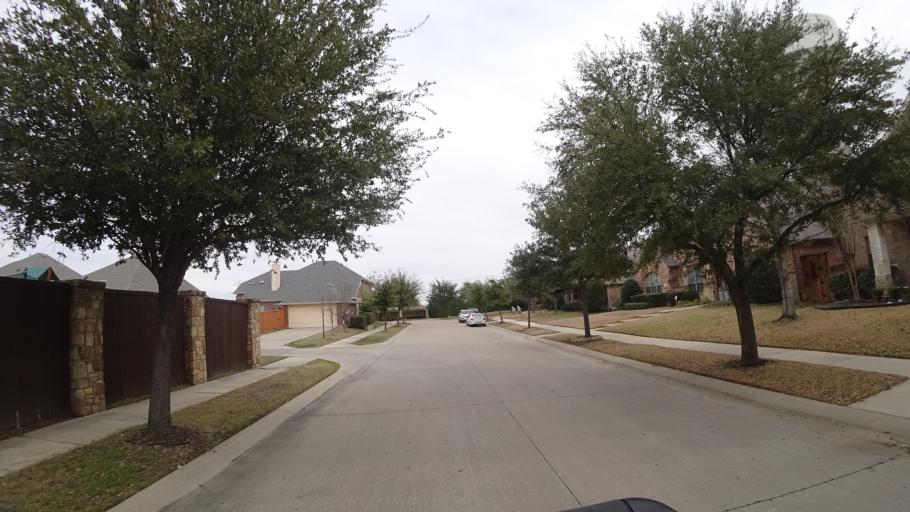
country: US
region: Texas
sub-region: Denton County
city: The Colony
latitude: 33.0444
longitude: -96.9089
